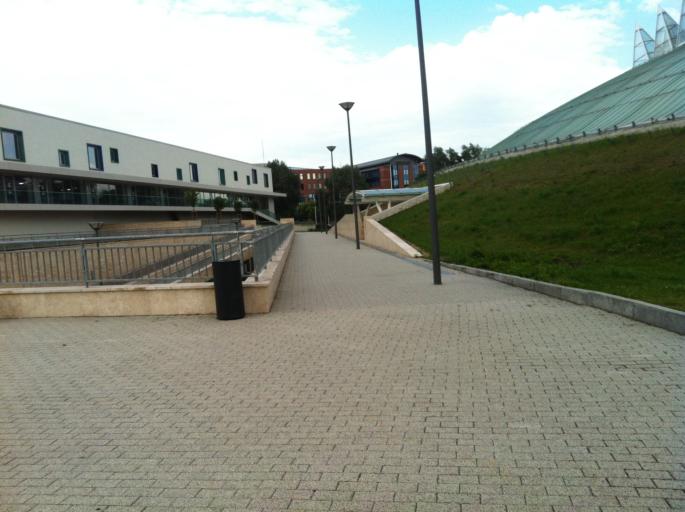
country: HU
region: Budapest
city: Budapest IX. keruelet
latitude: 47.4718
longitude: 19.0570
